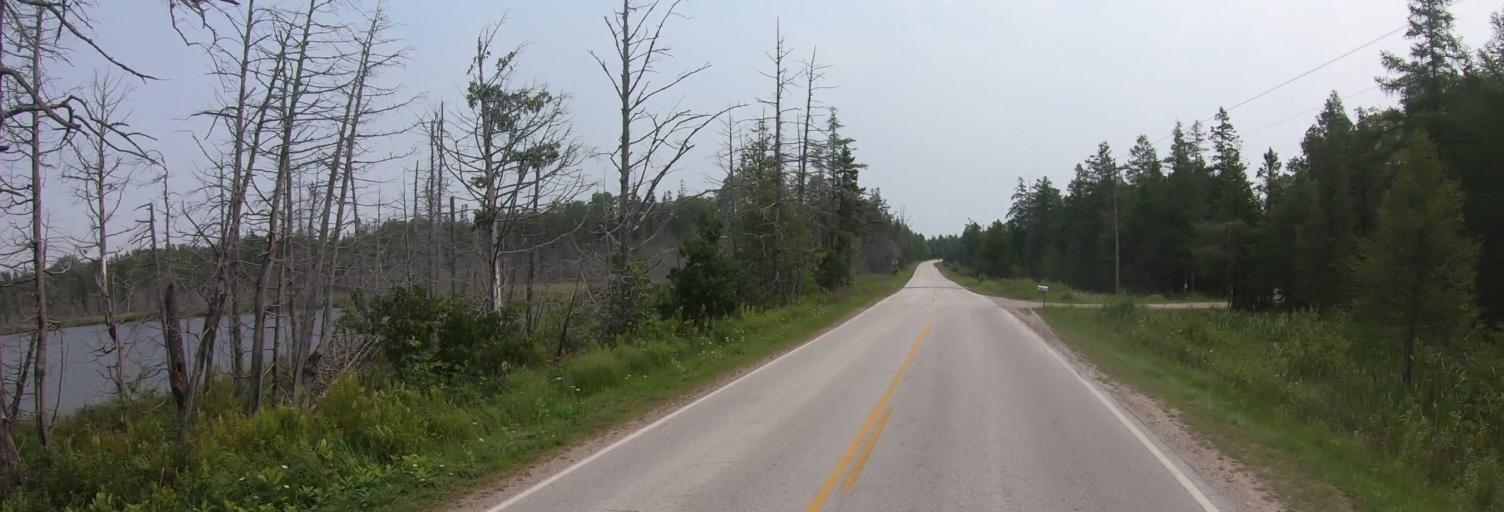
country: CA
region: Ontario
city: Thessalon
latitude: 45.9846
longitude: -83.6845
